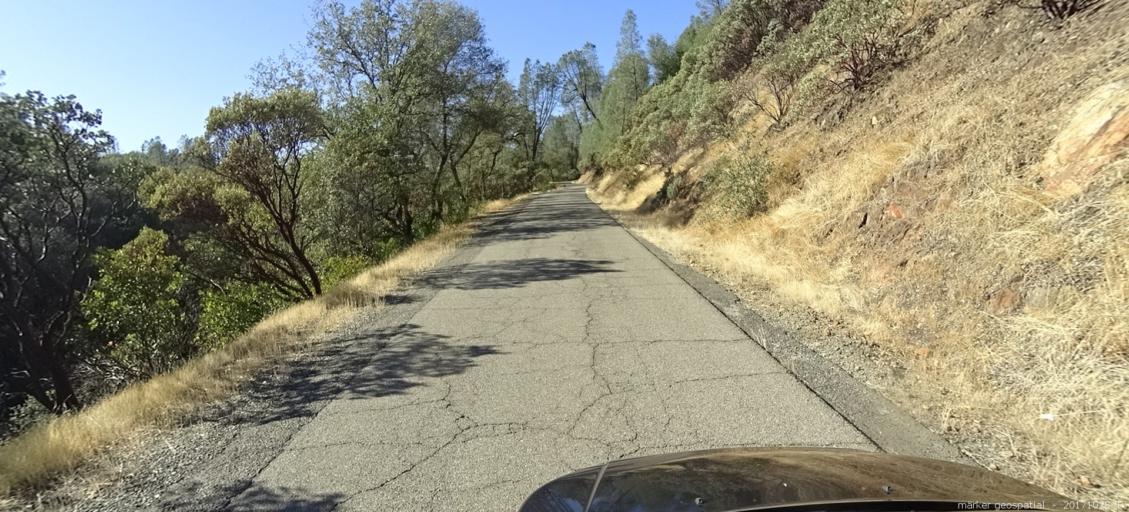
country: US
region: California
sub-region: Shasta County
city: Shasta
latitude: 40.5948
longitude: -122.4602
